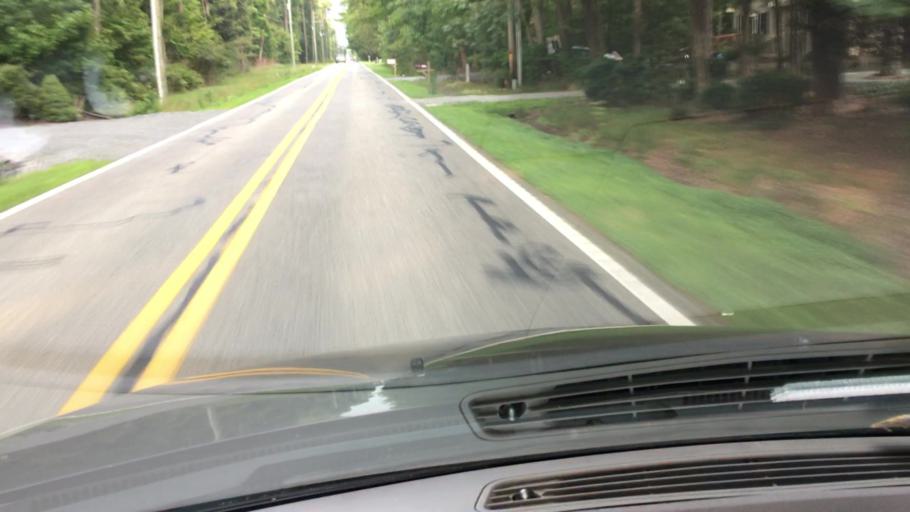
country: US
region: Delaware
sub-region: Sussex County
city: Ocean View
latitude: 38.5146
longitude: -75.0907
